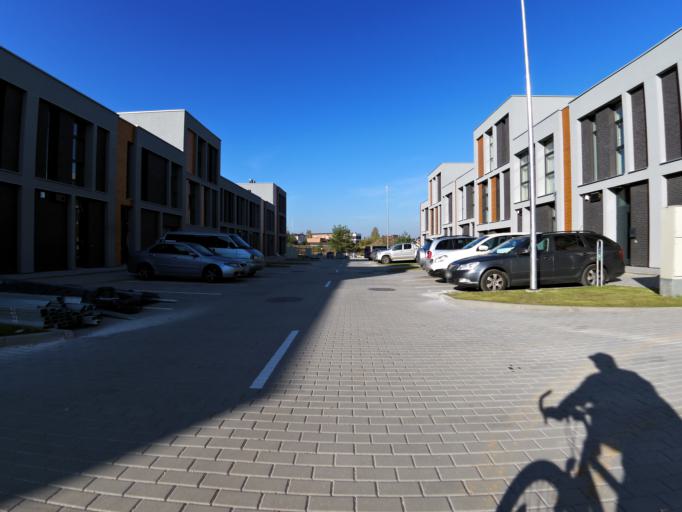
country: LT
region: Vilnius County
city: Pilaite
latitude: 54.7145
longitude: 25.1810
